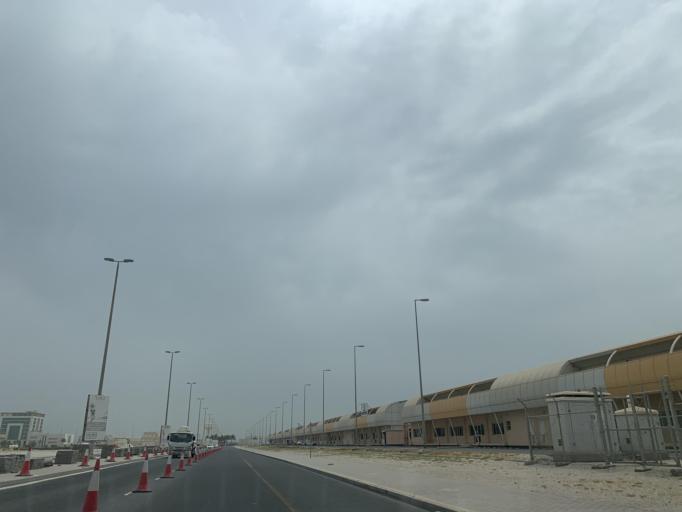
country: BH
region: Muharraq
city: Al Hadd
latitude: 26.2211
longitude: 50.6684
